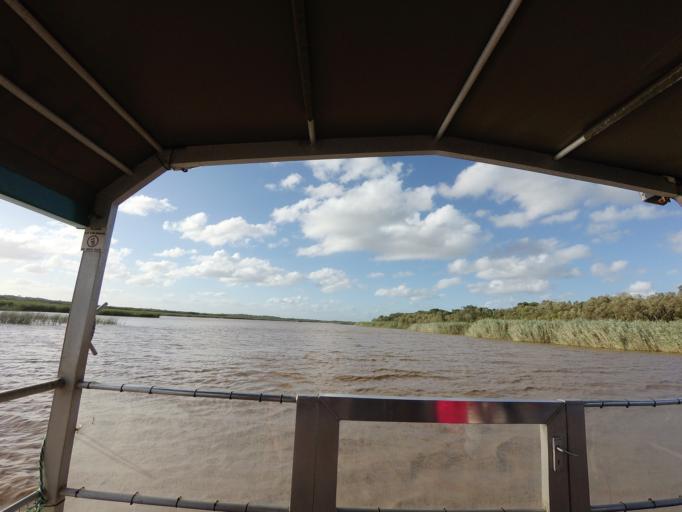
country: ZA
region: KwaZulu-Natal
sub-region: uMkhanyakude District Municipality
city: Mtubatuba
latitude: -28.3649
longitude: 32.4097
